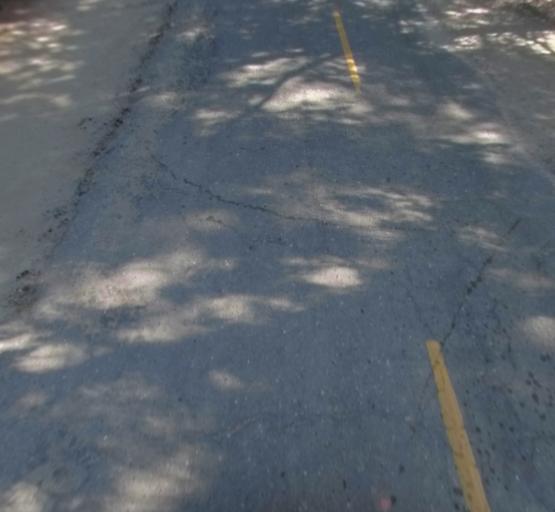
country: US
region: California
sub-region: Madera County
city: Chowchilla
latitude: 37.0865
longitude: -120.2613
